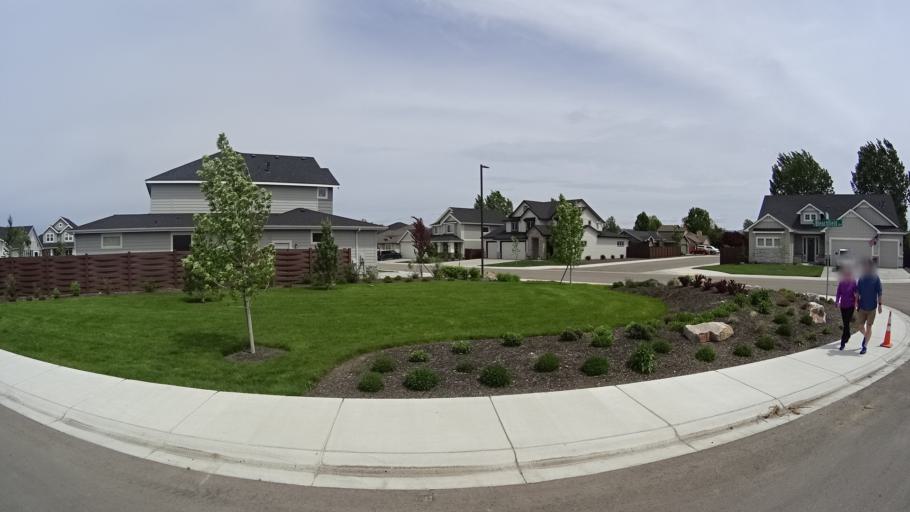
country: US
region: Idaho
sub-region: Ada County
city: Meridian
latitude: 43.5564
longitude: -116.3403
